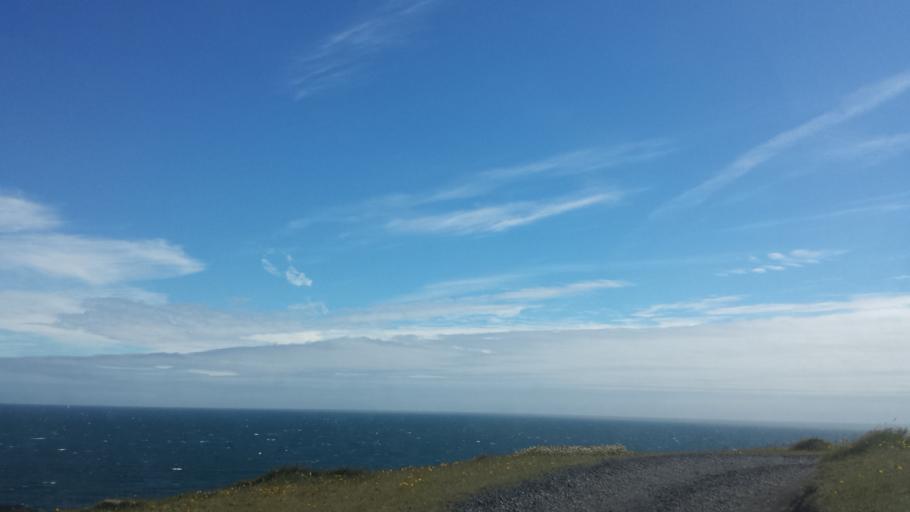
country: IS
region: South
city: Vestmannaeyjar
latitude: 63.4280
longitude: -20.2467
